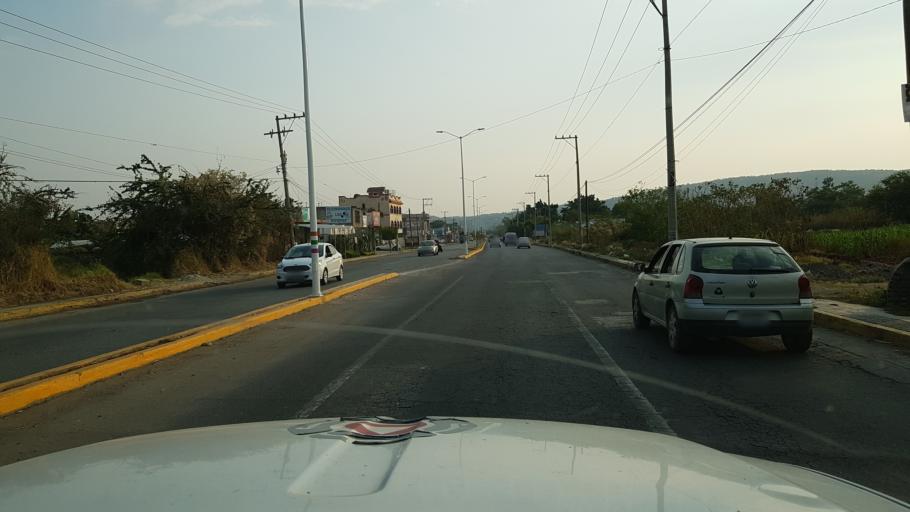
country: MX
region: Morelos
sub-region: Ayala
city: San Pedro Apatlaco
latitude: 18.7978
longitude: -98.9697
